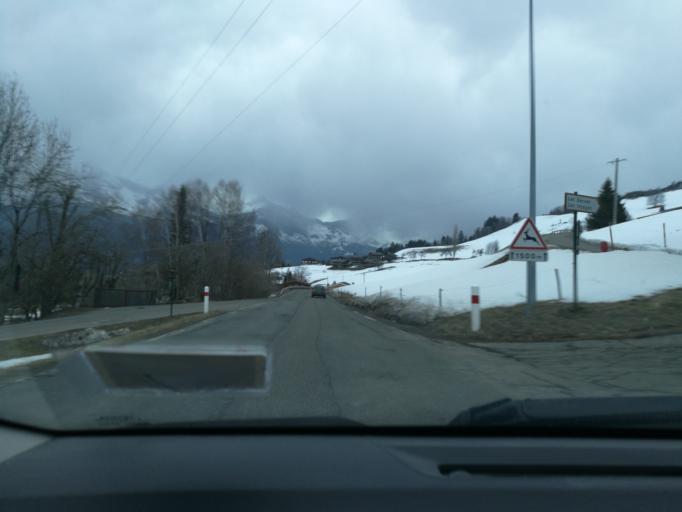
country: FR
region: Rhone-Alpes
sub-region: Departement de la Haute-Savoie
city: Combloux
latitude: 45.8844
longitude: 6.6470
